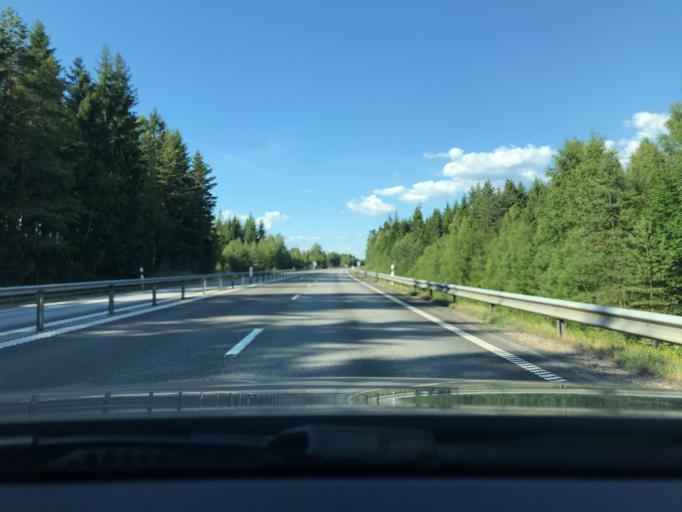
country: SE
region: Skane
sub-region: Osby Kommun
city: Osby
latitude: 56.4284
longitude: 14.0581
